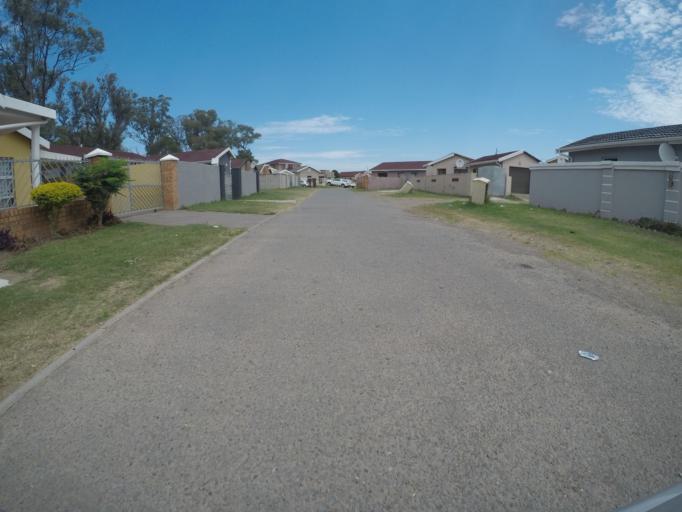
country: ZA
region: Eastern Cape
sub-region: Buffalo City Metropolitan Municipality
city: East London
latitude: -32.9914
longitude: 27.8690
